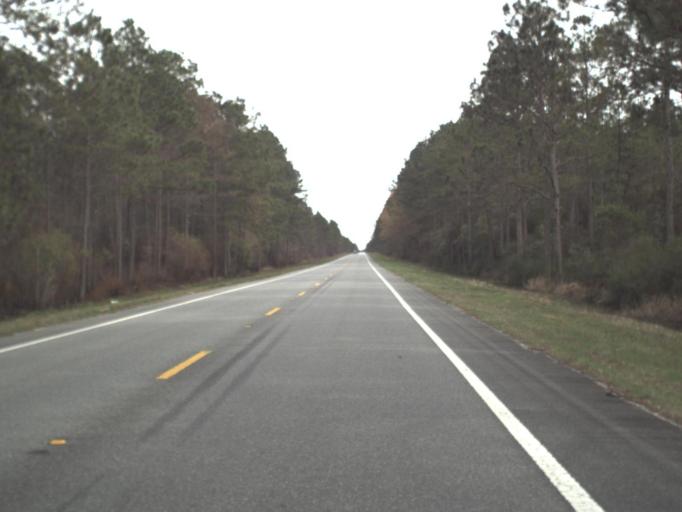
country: US
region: Florida
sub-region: Gadsden County
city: Midway
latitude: 30.3779
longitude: -84.5598
